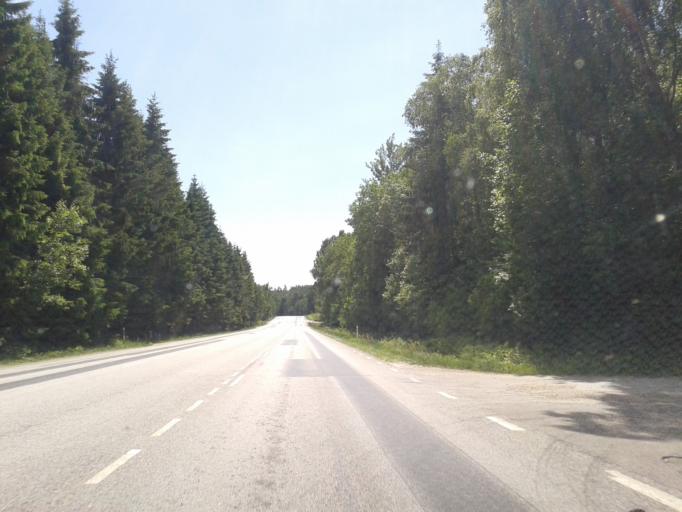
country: SE
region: Vaestra Goetaland
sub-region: Uddevalla Kommun
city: Ljungskile
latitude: 58.1211
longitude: 11.9861
